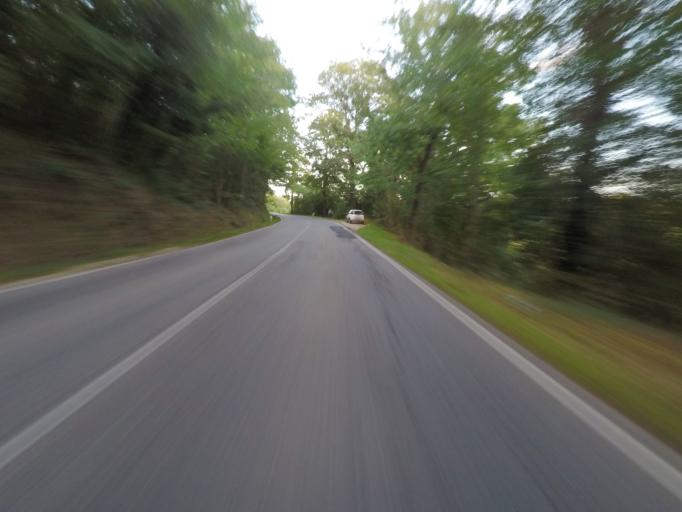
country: IT
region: Tuscany
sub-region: Provincia di Siena
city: Torrita di Siena
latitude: 43.1375
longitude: 11.7322
